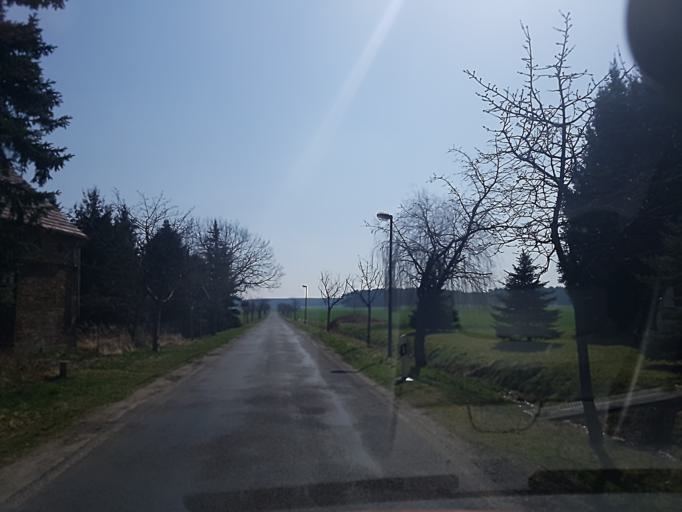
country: DE
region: Saxony
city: Gross Duben
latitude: 51.6732
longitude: 14.5372
